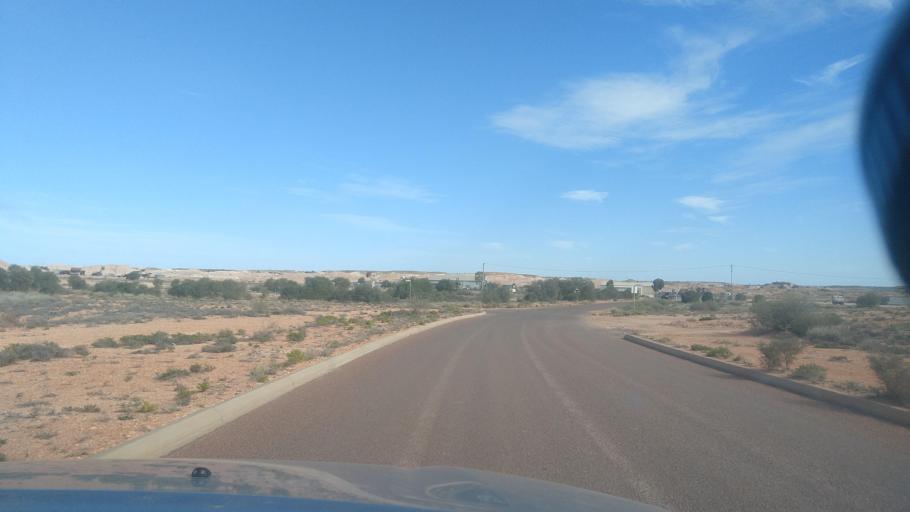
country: AU
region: South Australia
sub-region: Coober Pedy
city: Coober Pedy
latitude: -29.0142
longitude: 134.7480
